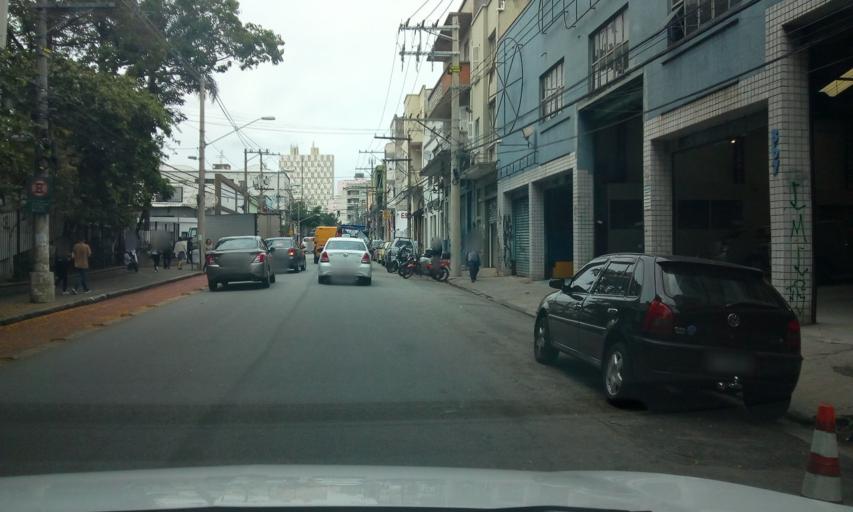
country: BR
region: Sao Paulo
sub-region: Sao Paulo
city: Sao Paulo
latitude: -23.5276
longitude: -46.6586
